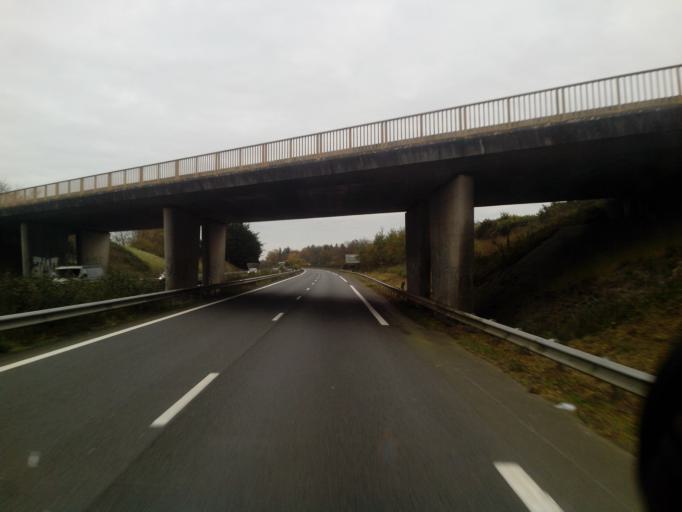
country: FR
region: Pays de la Loire
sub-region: Departement de la Loire-Atlantique
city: Haute-Goulaine
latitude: 47.1810
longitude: -1.4124
